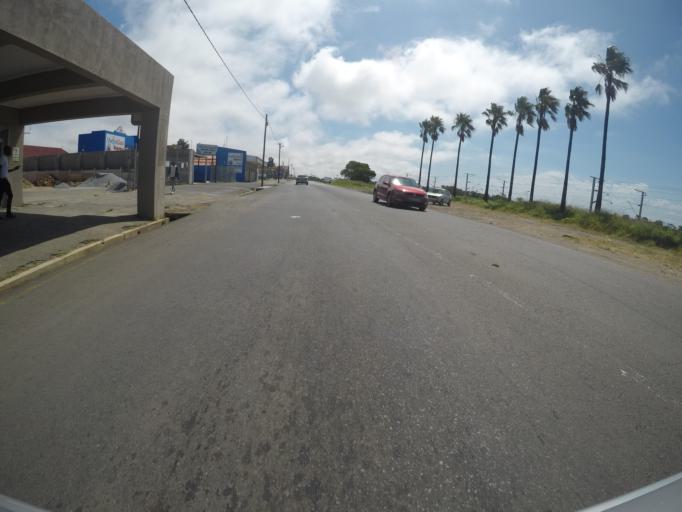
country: ZA
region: Eastern Cape
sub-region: Buffalo City Metropolitan Municipality
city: East London
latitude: -32.9743
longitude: 27.8954
